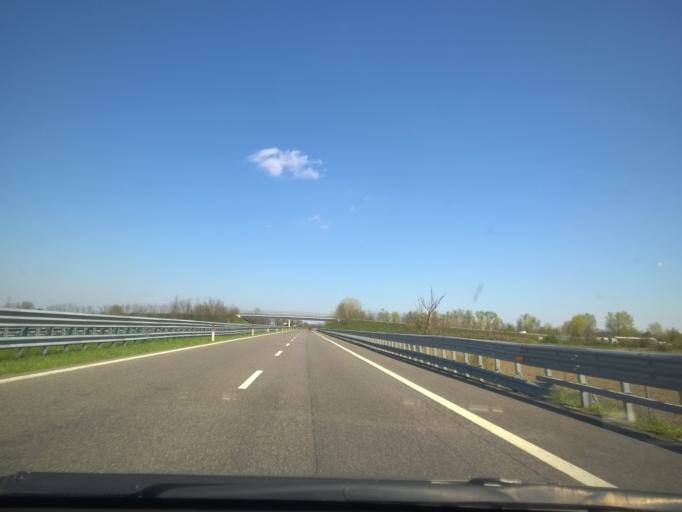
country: IT
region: Emilia-Romagna
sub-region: Provincia di Piacenza
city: Pontenure
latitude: 45.0451
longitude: 9.8190
